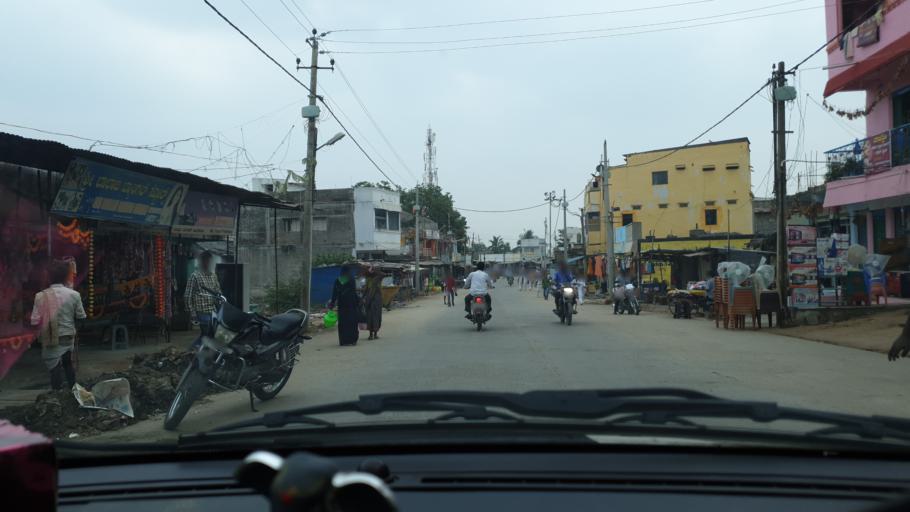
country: IN
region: Karnataka
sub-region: Yadgir
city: Gurmatkal
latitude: 16.8681
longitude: 77.3918
